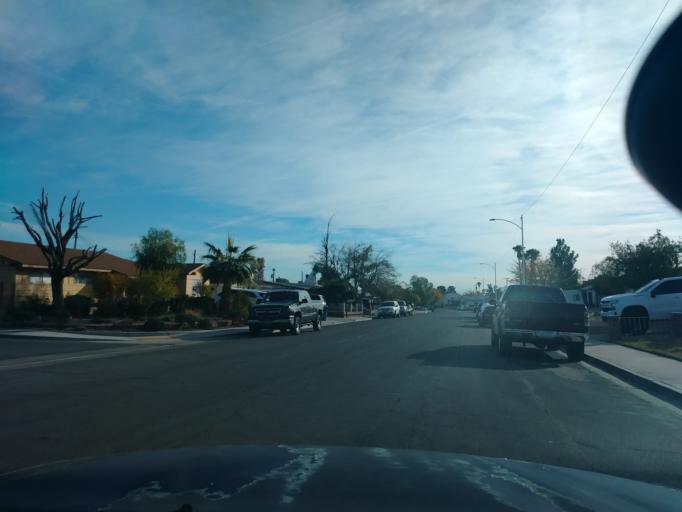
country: US
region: Nevada
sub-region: Clark County
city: Spring Valley
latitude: 36.1634
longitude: -115.2386
